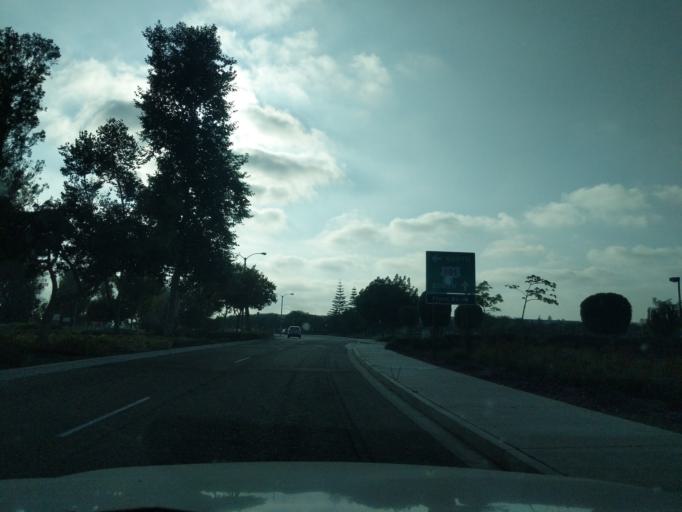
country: US
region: California
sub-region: Ventura County
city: Camarillo
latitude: 34.2164
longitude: -119.0201
